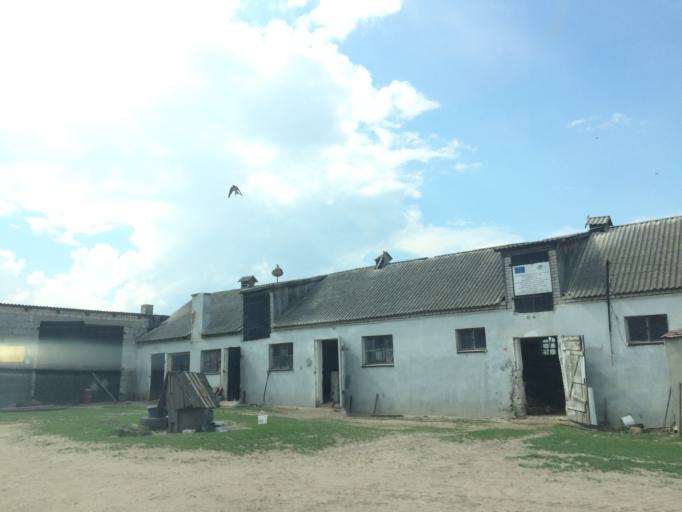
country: PL
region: Warmian-Masurian Voivodeship
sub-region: Powiat nowomiejski
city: Biskupiec
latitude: 53.5297
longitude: 19.4257
